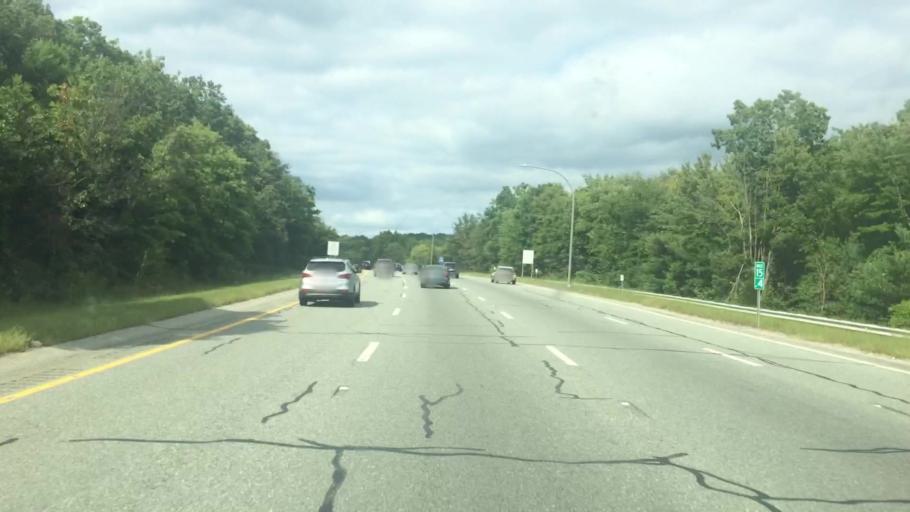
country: US
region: Rhode Island
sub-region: Providence County
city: Smithfield
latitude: 41.9122
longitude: -71.5079
